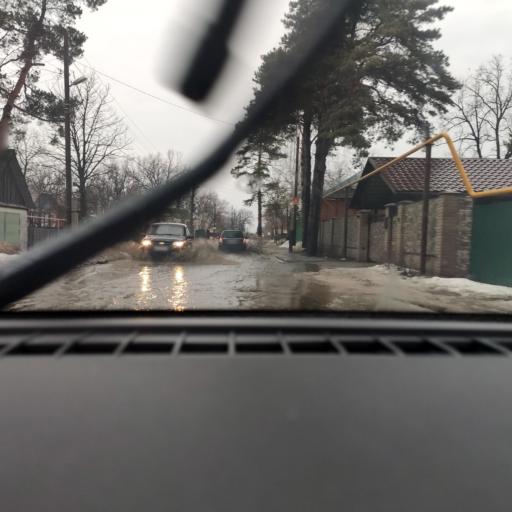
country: RU
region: Voronezj
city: Somovo
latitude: 51.7344
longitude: 39.3583
